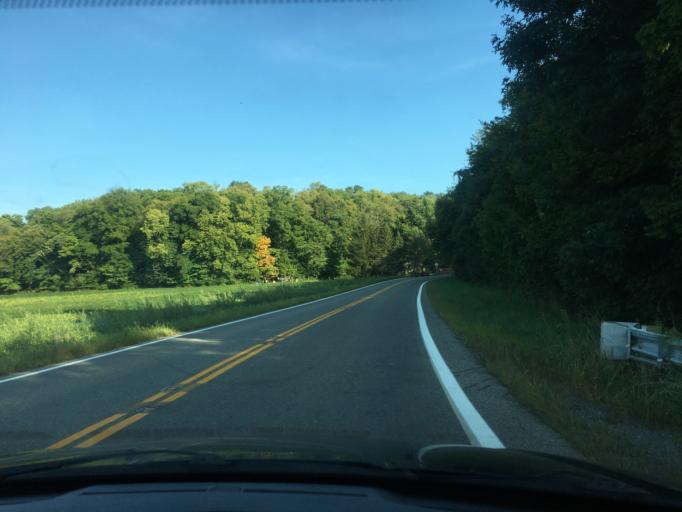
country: US
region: Ohio
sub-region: Logan County
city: West Liberty
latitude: 40.2653
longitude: -83.6661
